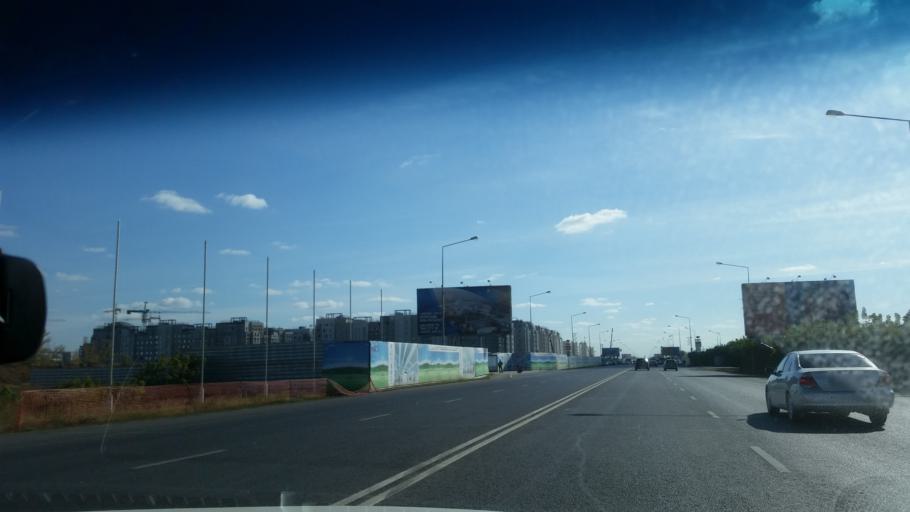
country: KZ
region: Astana Qalasy
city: Astana
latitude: 51.1015
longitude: 71.4070
